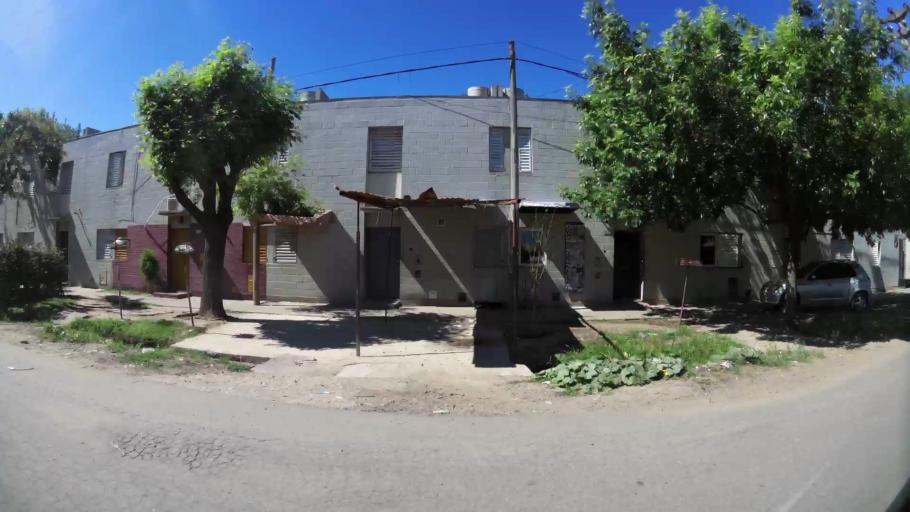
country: AR
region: Santa Fe
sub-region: Departamento de Rosario
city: Rosario
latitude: -32.9746
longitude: -60.6973
